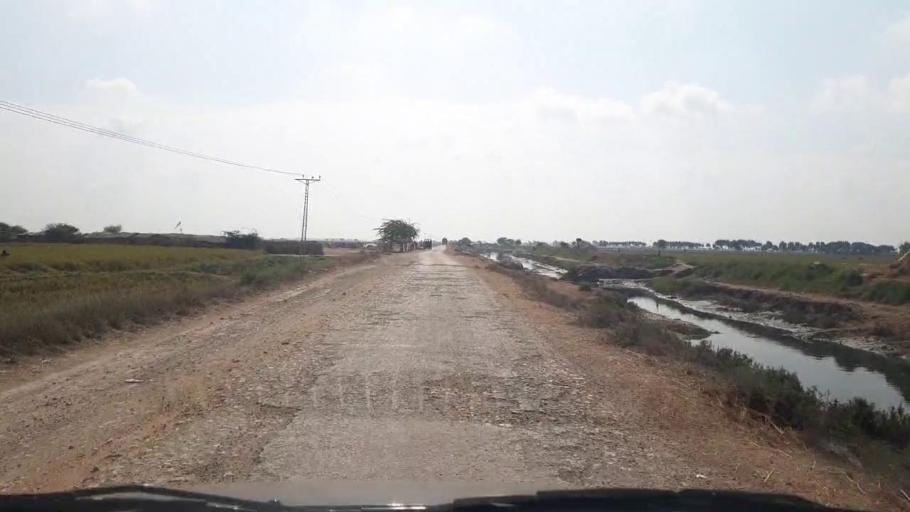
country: PK
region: Sindh
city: Kario
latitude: 24.6295
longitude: 68.5516
